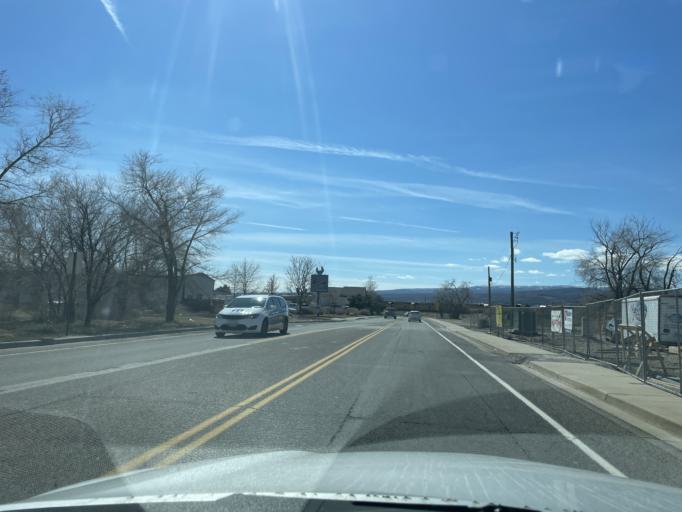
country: US
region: Colorado
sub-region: Mesa County
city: Grand Junction
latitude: 39.0744
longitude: -108.5803
